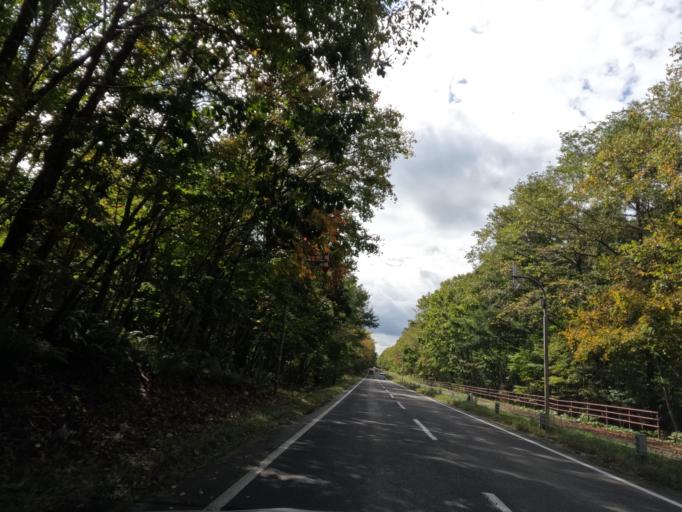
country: JP
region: Hokkaido
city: Chitose
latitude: 42.7944
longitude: 141.5591
